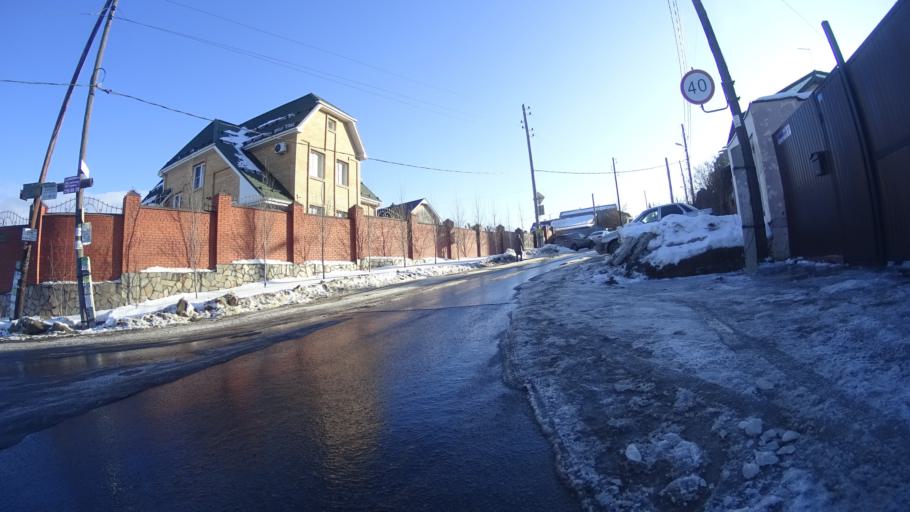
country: RU
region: Chelyabinsk
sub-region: Gorod Chelyabinsk
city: Chelyabinsk
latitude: 55.1540
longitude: 61.3104
